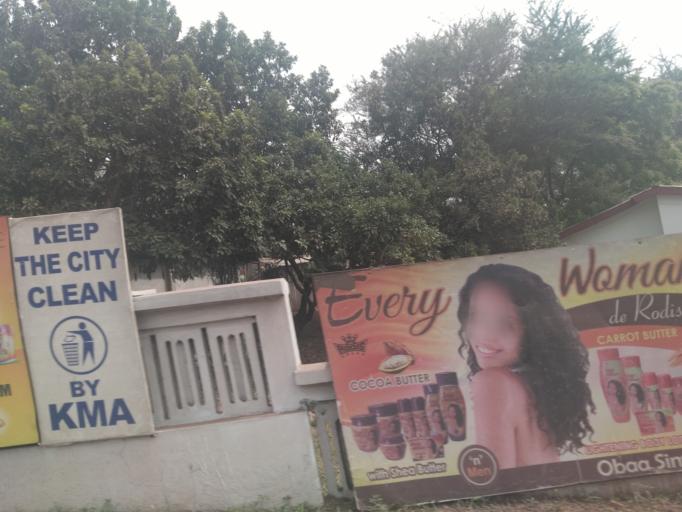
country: GH
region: Ashanti
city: Kumasi
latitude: 6.6854
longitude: -1.6234
